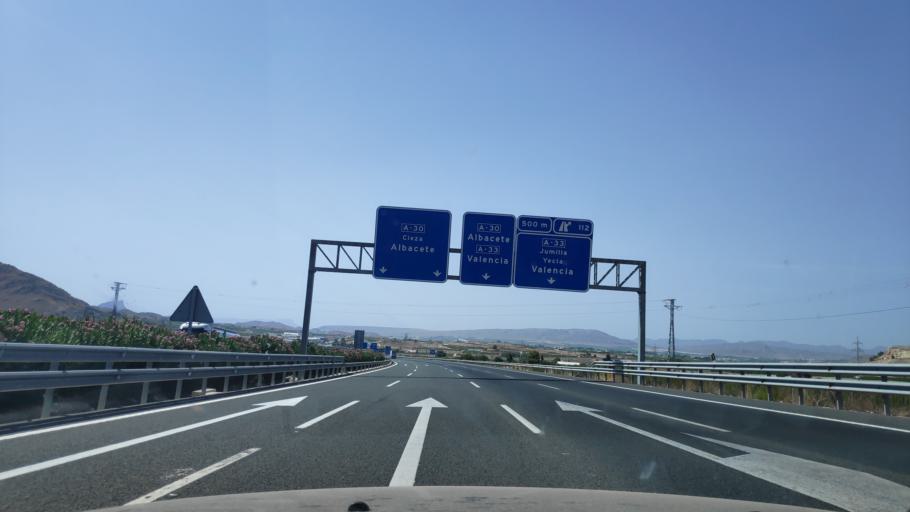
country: ES
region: Murcia
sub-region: Murcia
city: Ojos
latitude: 38.1816
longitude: -1.3174
